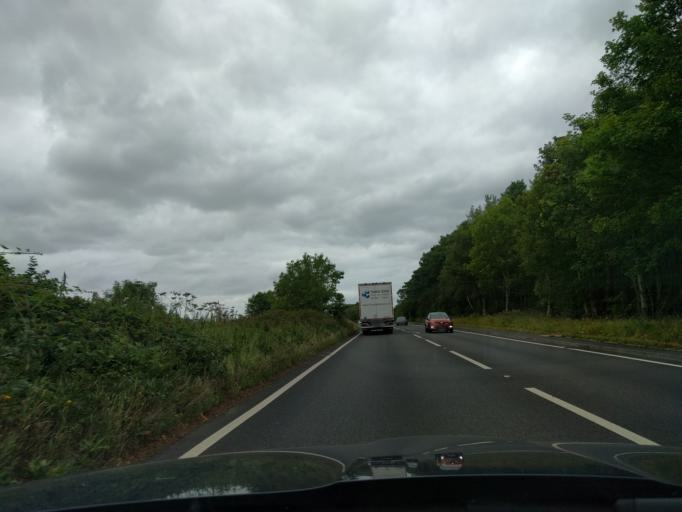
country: GB
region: England
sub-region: Northumberland
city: Ancroft
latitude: 55.7280
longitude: -1.9860
